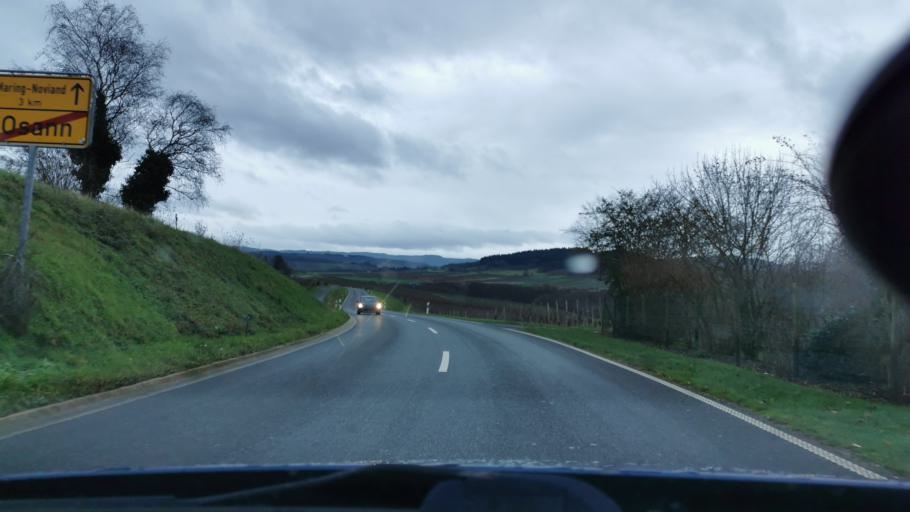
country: DE
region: Rheinland-Pfalz
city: Osann-Monzel
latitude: 49.9203
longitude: 6.9585
